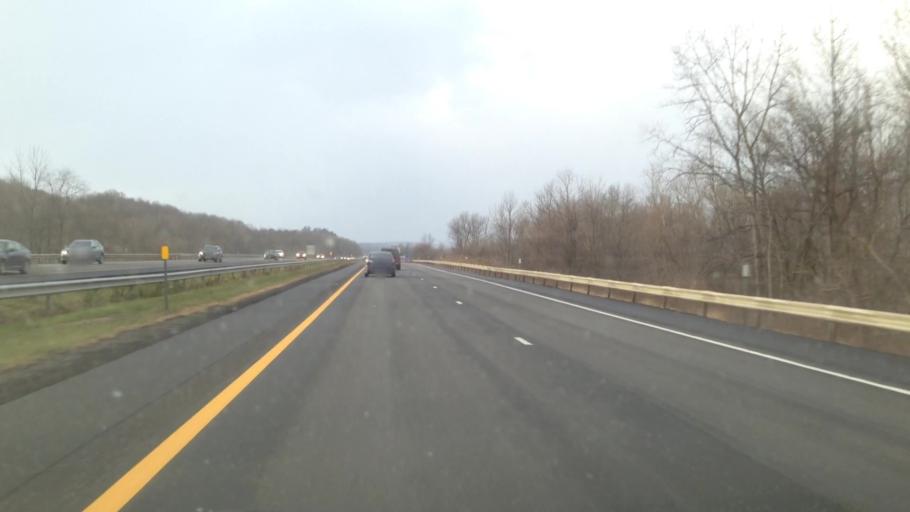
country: US
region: New York
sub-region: Montgomery County
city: Tribes Hill
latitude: 42.9344
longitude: -74.3224
